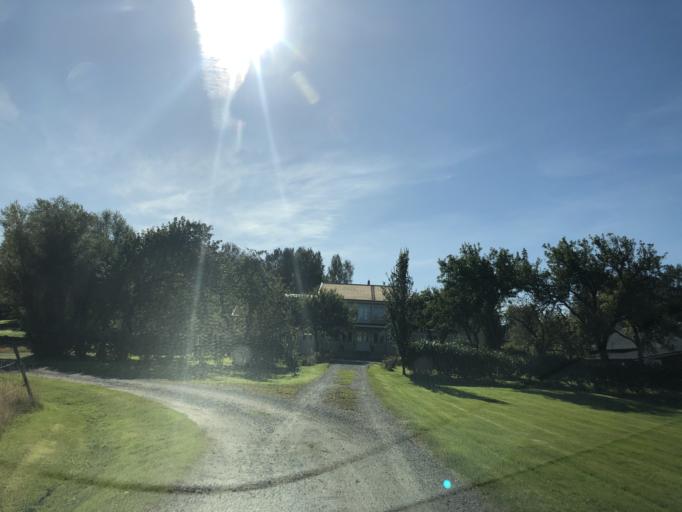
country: SE
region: Vaestra Goetaland
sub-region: Goteborg
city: Majorna
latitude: 57.7712
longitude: 11.9153
